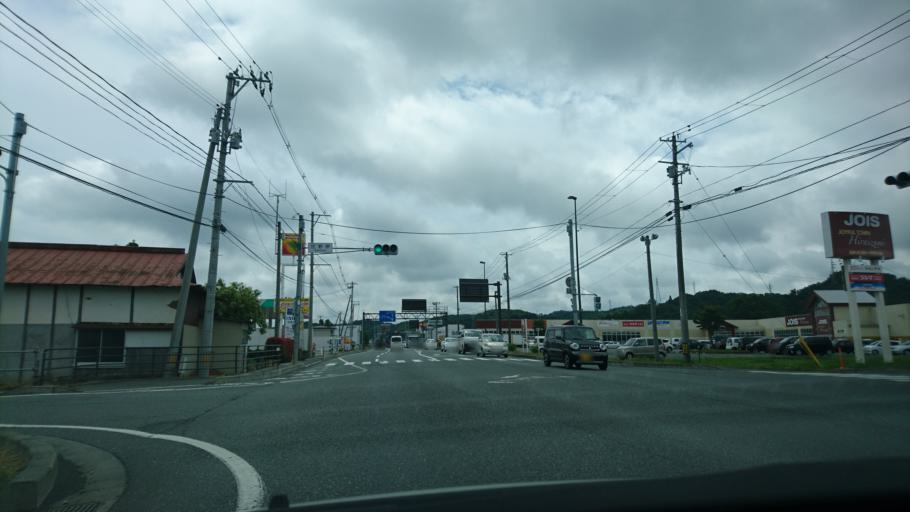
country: JP
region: Iwate
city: Ichinoseki
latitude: 38.9717
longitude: 141.1184
